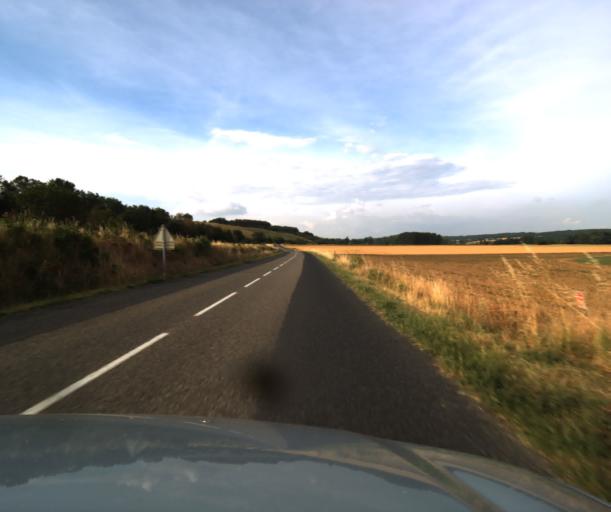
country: FR
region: Midi-Pyrenees
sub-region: Departement du Tarn-et-Garonne
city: Castelsarrasin
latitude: 43.9596
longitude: 1.1040
